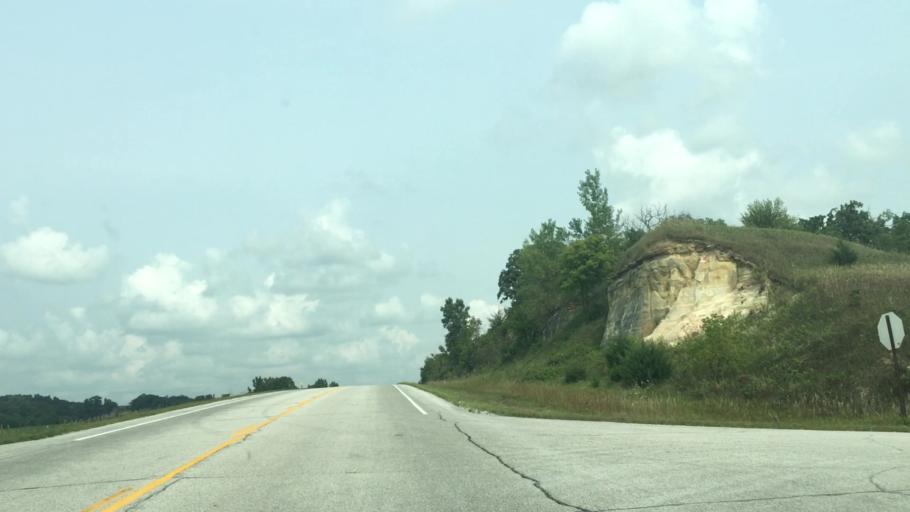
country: US
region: Minnesota
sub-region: Fillmore County
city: Harmony
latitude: 43.6270
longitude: -91.9299
